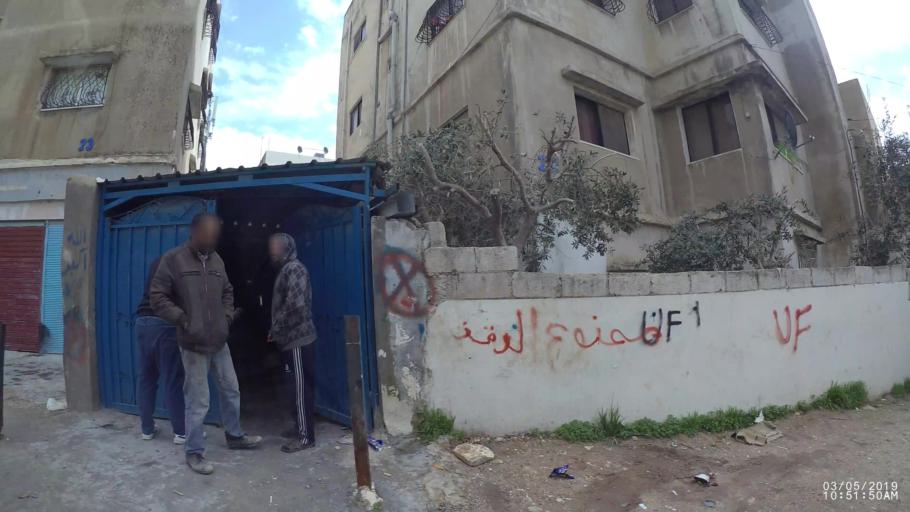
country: JO
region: Amman
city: Amman
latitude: 31.9817
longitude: 35.9203
